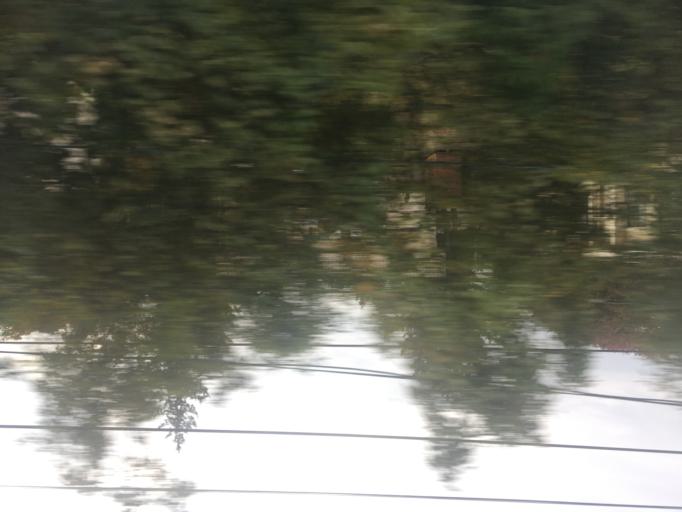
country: JP
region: Tokyo
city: Fussa
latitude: 35.7532
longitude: 139.3389
